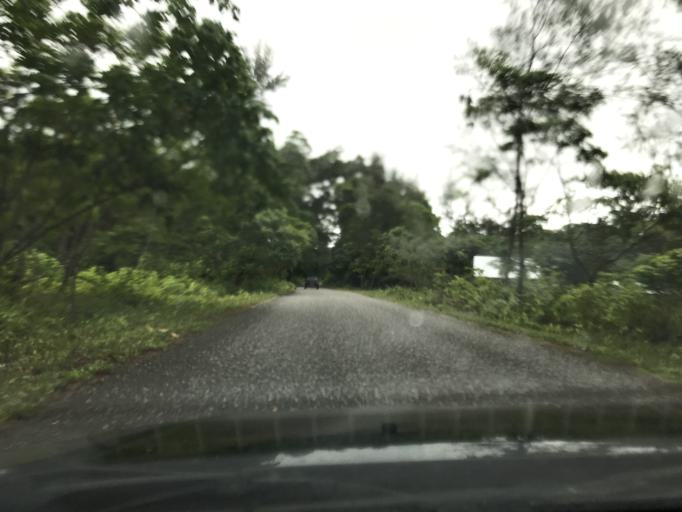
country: SB
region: Western Province
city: Gizo
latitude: -8.3256
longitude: 157.2586
